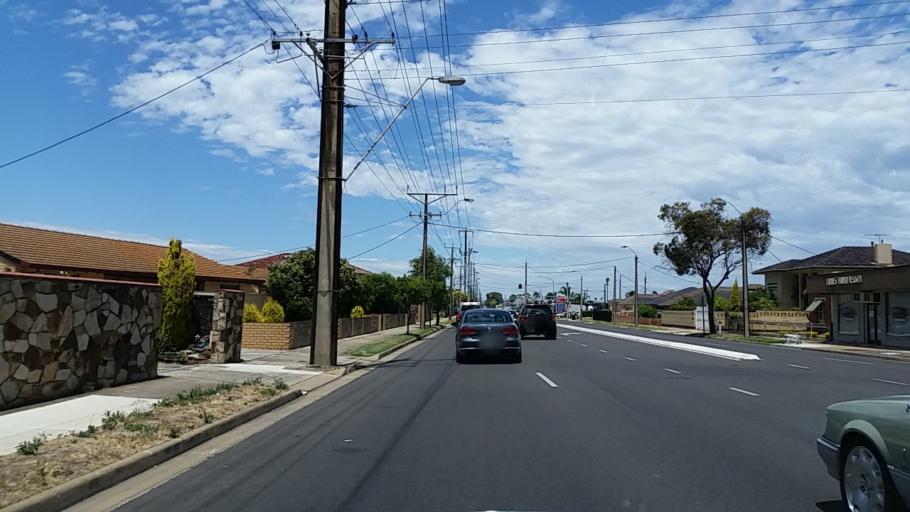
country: AU
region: South Australia
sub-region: Charles Sturt
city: Woodville West
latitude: -34.8893
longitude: 138.5315
